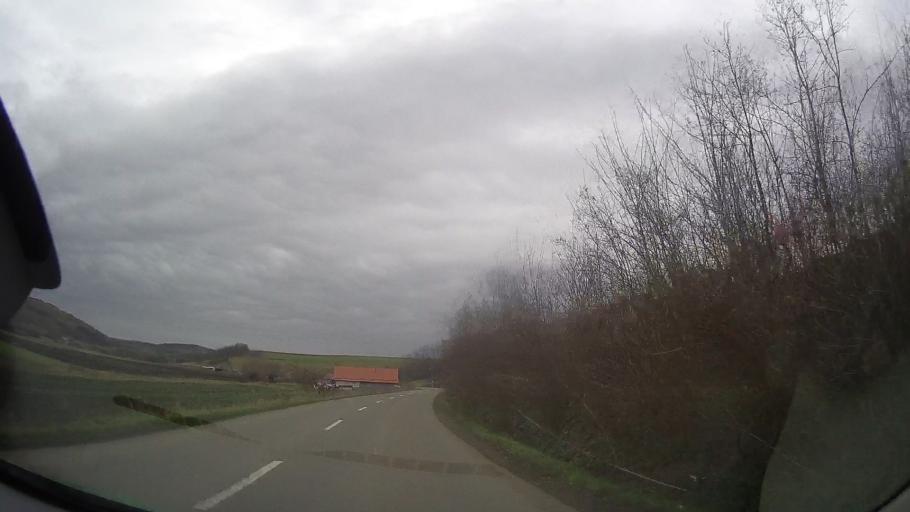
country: RO
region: Mures
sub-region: Comuna Craesti
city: Craiesti
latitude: 46.7742
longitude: 24.4256
